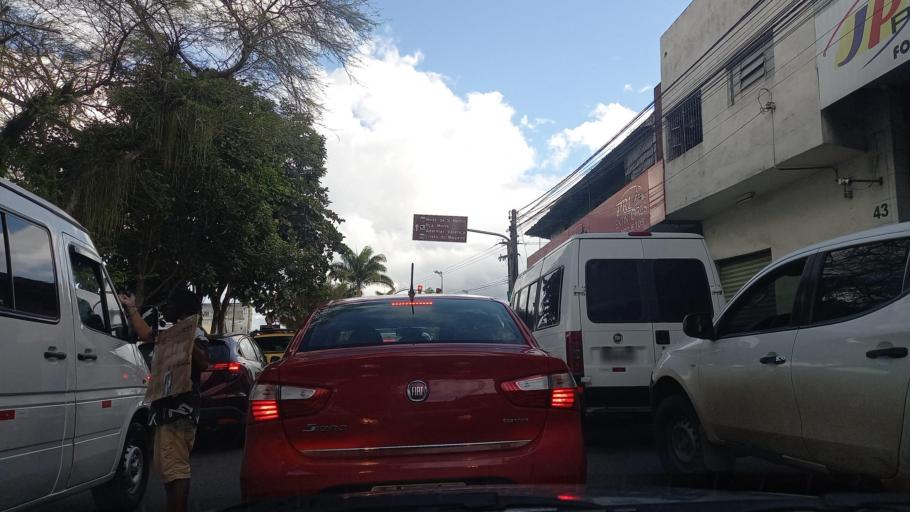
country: BR
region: Pernambuco
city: Garanhuns
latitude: -8.8859
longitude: -36.4898
